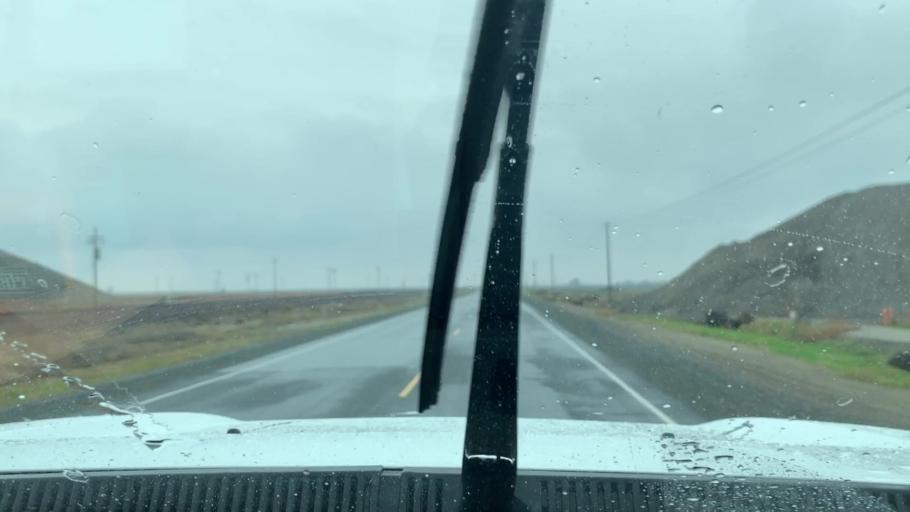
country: US
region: California
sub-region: Tulare County
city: Alpaugh
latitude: 35.9469
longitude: -119.4458
